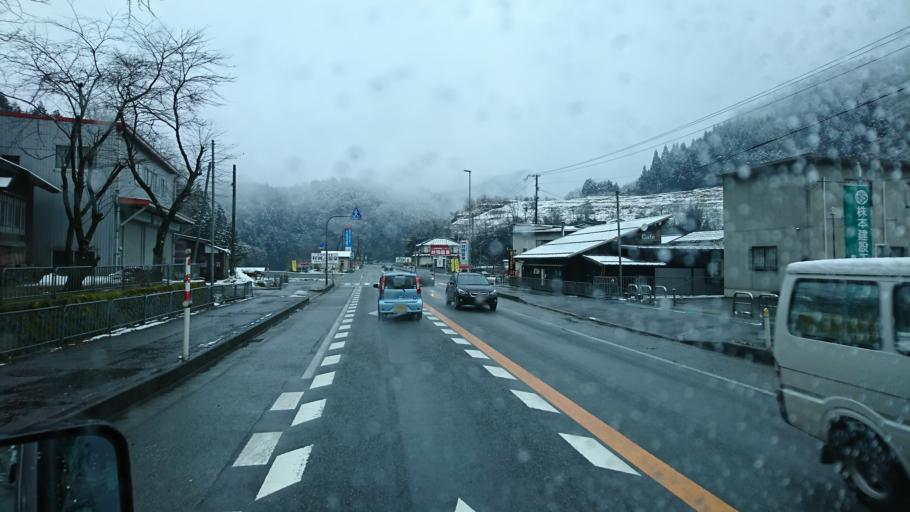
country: JP
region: Hyogo
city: Toyooka
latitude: 35.4754
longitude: 134.5871
